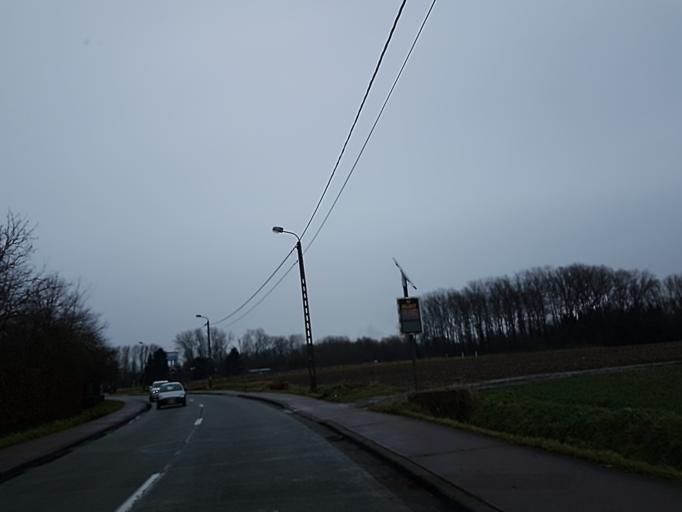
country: BE
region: Flanders
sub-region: Provincie Antwerpen
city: Puurs
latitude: 51.0723
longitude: 4.2634
